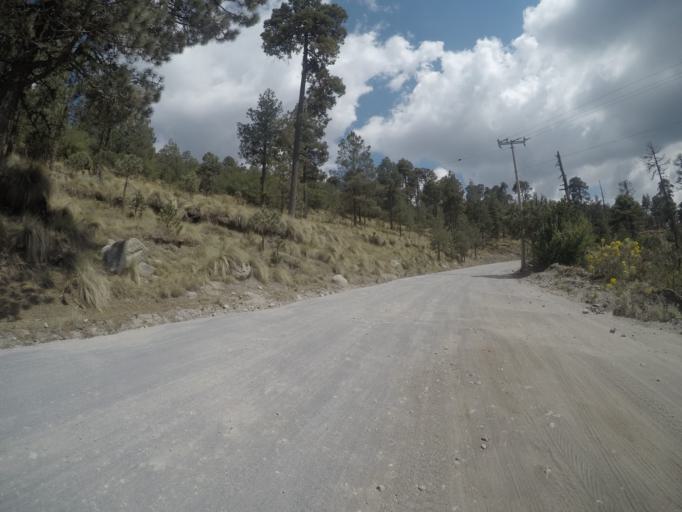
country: MX
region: Mexico
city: Cerro La Calera
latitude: 19.1400
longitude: -99.7998
